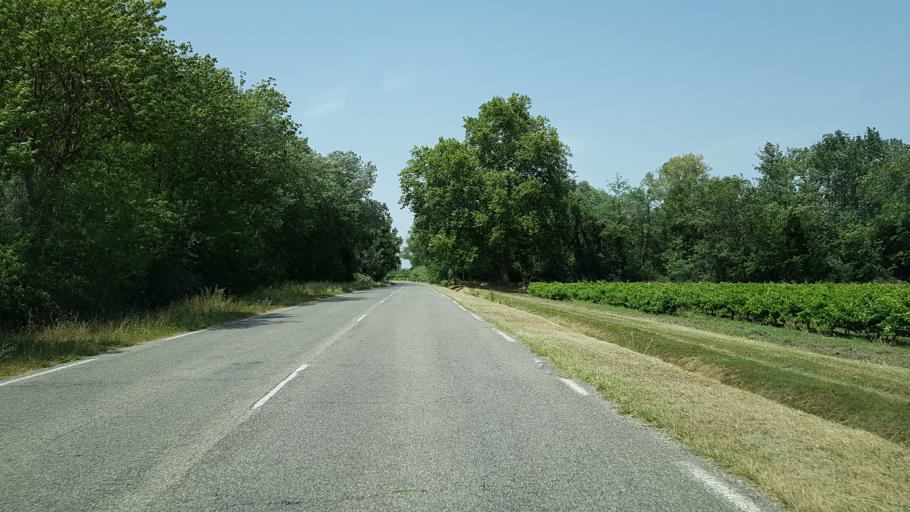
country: FR
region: Provence-Alpes-Cote d'Azur
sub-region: Departement des Bouches-du-Rhone
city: Saint-Martin-de-Crau
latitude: 43.5250
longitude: 4.7403
